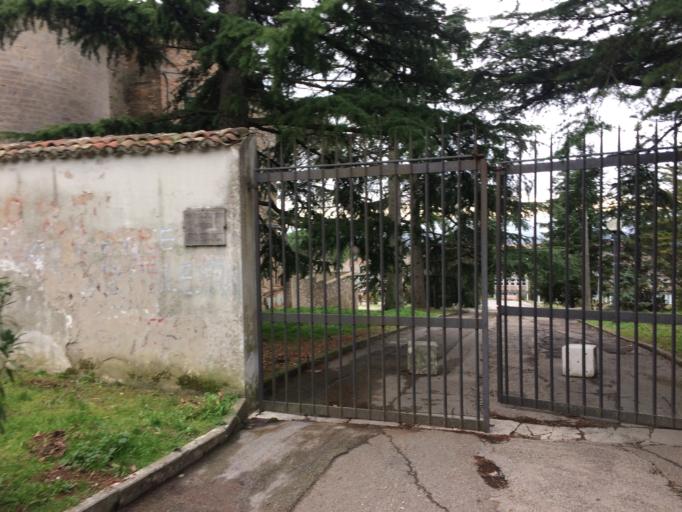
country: IT
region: Umbria
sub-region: Provincia di Perugia
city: Perugia
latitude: 43.0989
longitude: 12.3964
